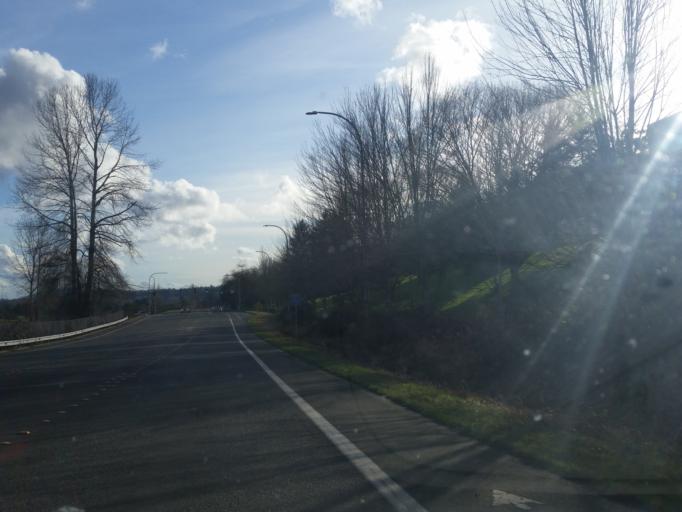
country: US
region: Washington
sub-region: King County
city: Kingsgate
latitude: 47.7062
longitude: -122.1537
